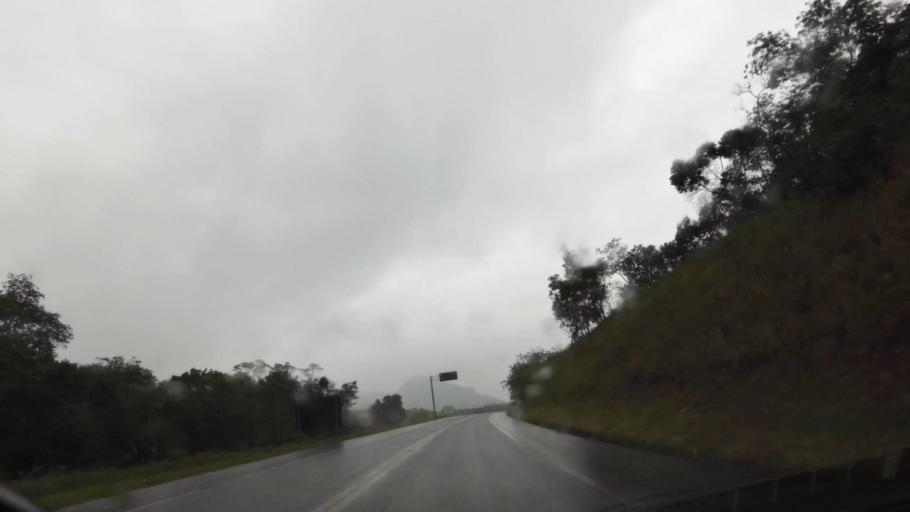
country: BR
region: Espirito Santo
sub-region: Guarapari
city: Guarapari
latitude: -20.6348
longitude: -40.5258
